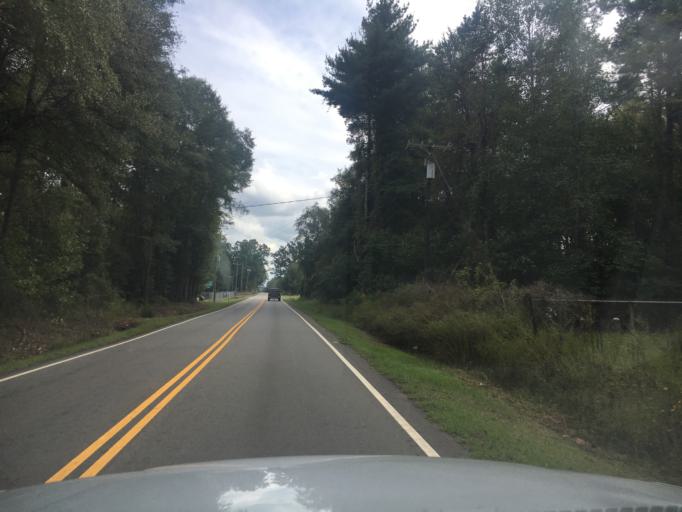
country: US
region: South Carolina
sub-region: Spartanburg County
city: Wellford
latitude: 34.9223
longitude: -82.0623
